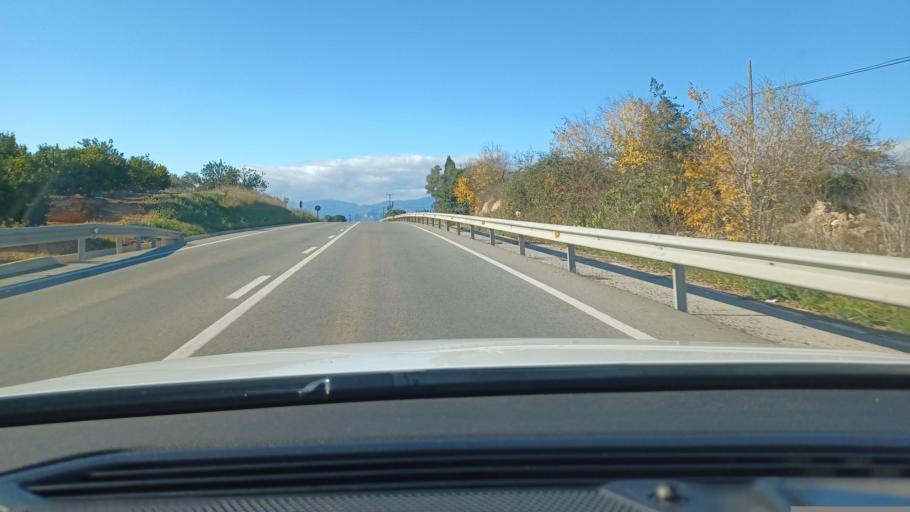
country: ES
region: Catalonia
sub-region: Provincia de Tarragona
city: Masdenverge
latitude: 40.7172
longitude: 0.5210
